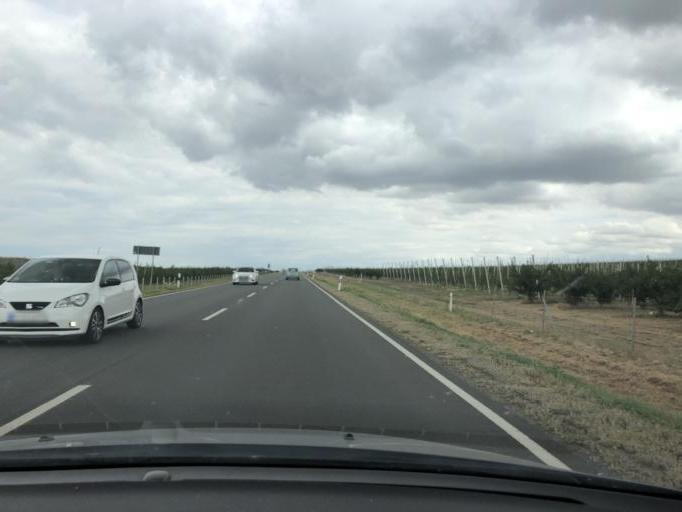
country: DE
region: Saxony-Anhalt
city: Erdeborn
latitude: 51.4936
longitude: 11.6490
